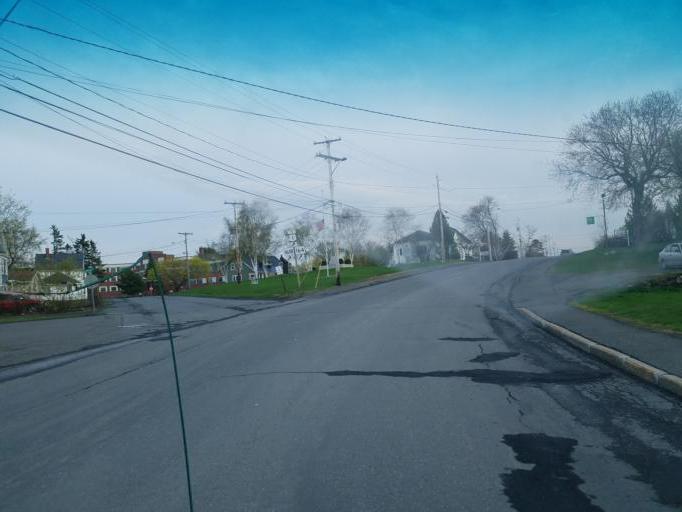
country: US
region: Maine
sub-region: Aroostook County
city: Caribou
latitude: 46.8587
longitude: -68.0106
